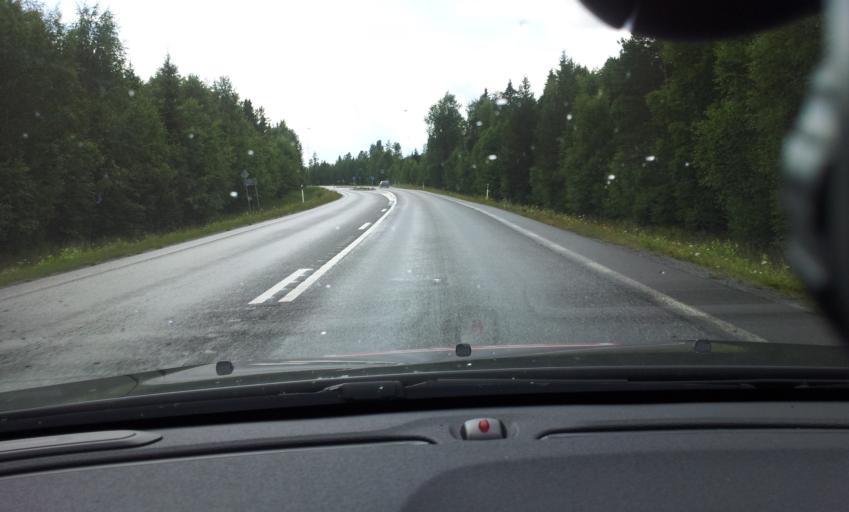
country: SE
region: Jaemtland
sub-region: Krokoms Kommun
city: Krokom
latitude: 63.3231
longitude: 14.1953
